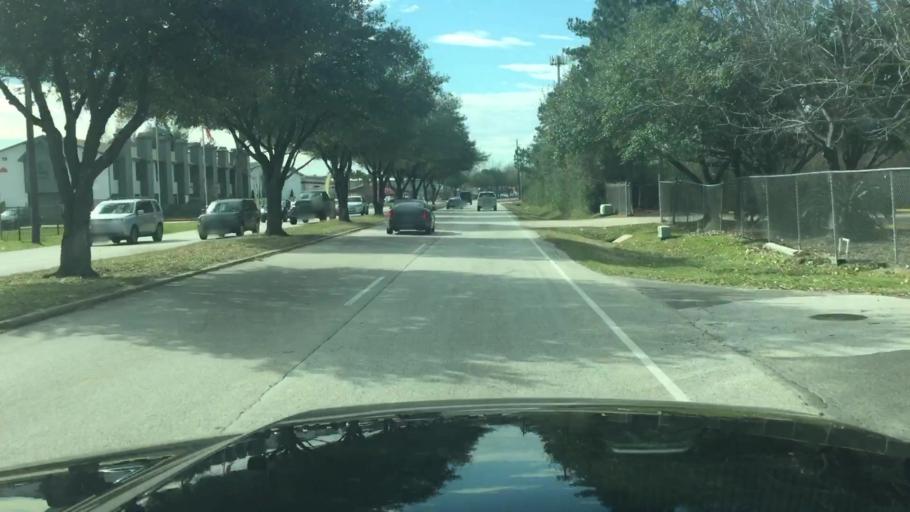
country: US
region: Texas
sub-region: Harris County
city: Oak Cliff Place
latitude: 29.8337
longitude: -95.6577
